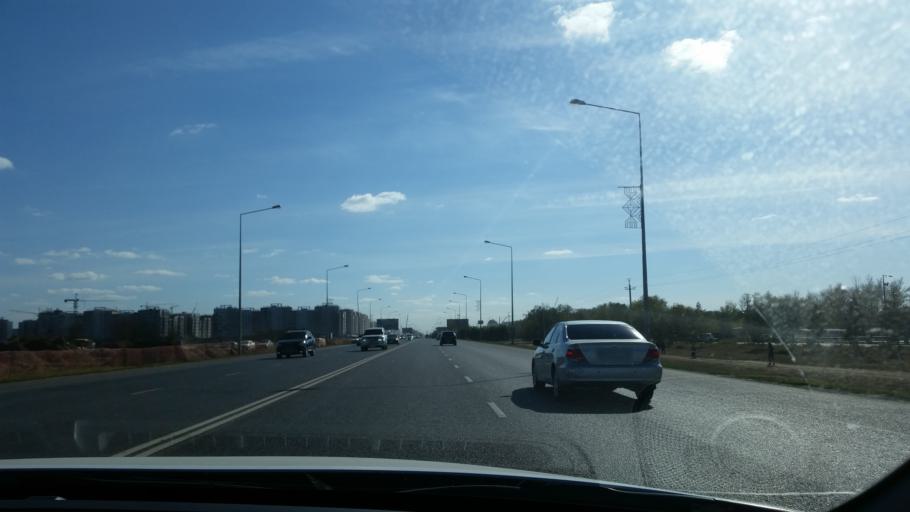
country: KZ
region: Astana Qalasy
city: Astana
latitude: 51.1040
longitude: 71.4078
